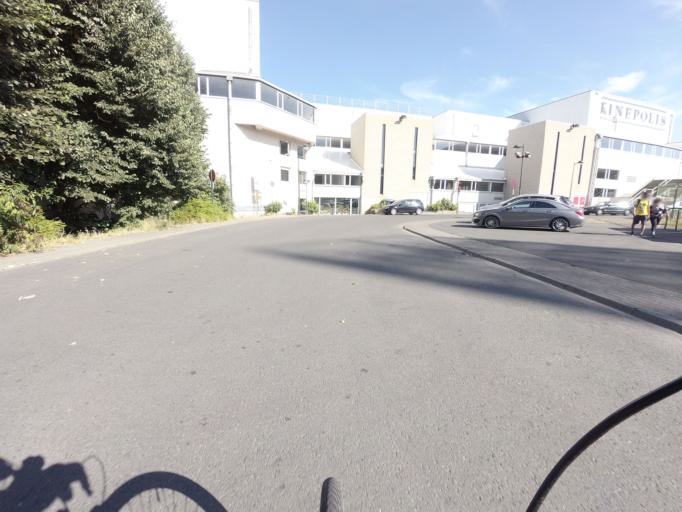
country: BE
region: Flanders
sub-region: Provincie Vlaams-Brabant
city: Bever
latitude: 50.8958
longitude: 4.3367
